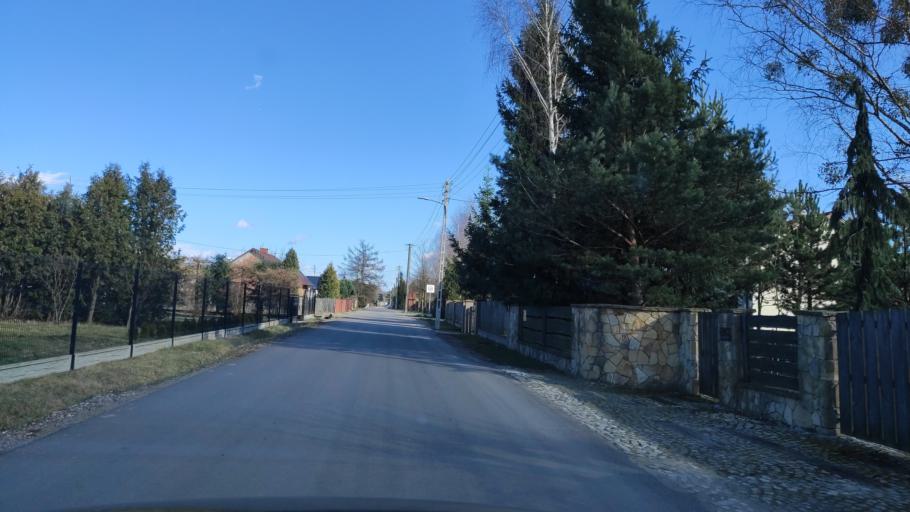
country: PL
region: Masovian Voivodeship
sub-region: Powiat radomski
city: Jedlnia-Letnisko
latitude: 51.4397
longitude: 21.2995
